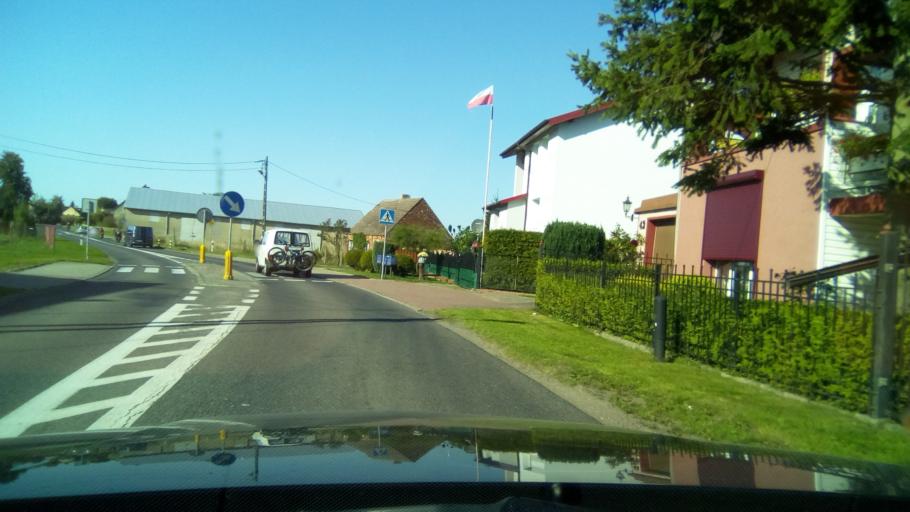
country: PL
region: West Pomeranian Voivodeship
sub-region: Powiat kamienski
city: Golczewo
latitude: 53.8250
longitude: 14.8957
